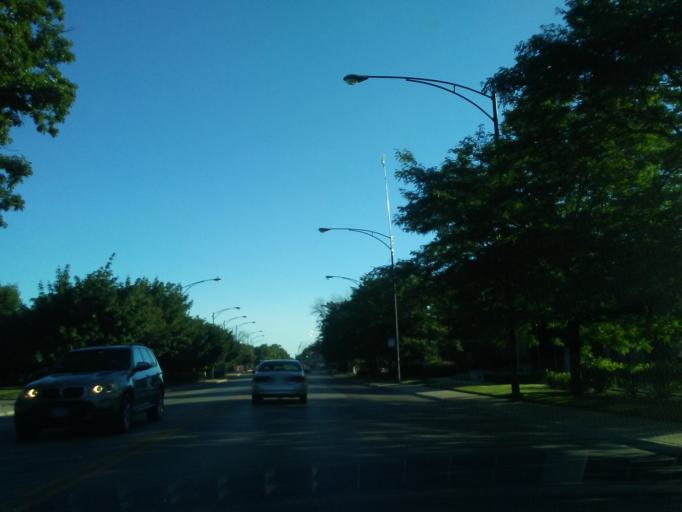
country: US
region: Illinois
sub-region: Cook County
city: Lincolnwood
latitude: 41.9733
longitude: -87.7282
